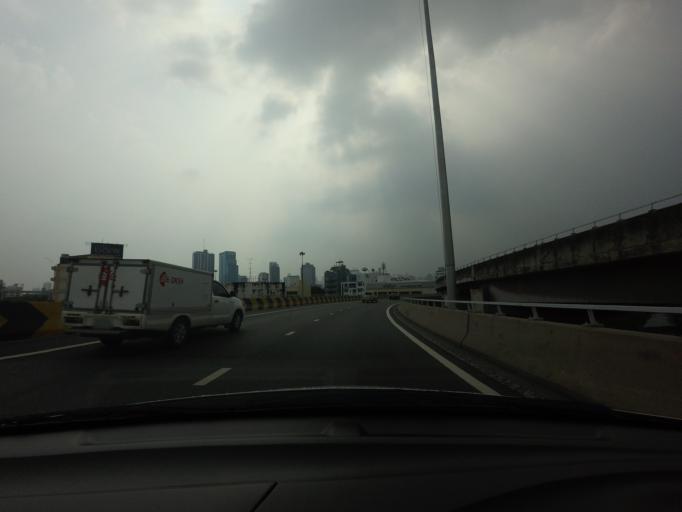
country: TH
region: Bangkok
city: Watthana
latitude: 13.7501
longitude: 100.5937
